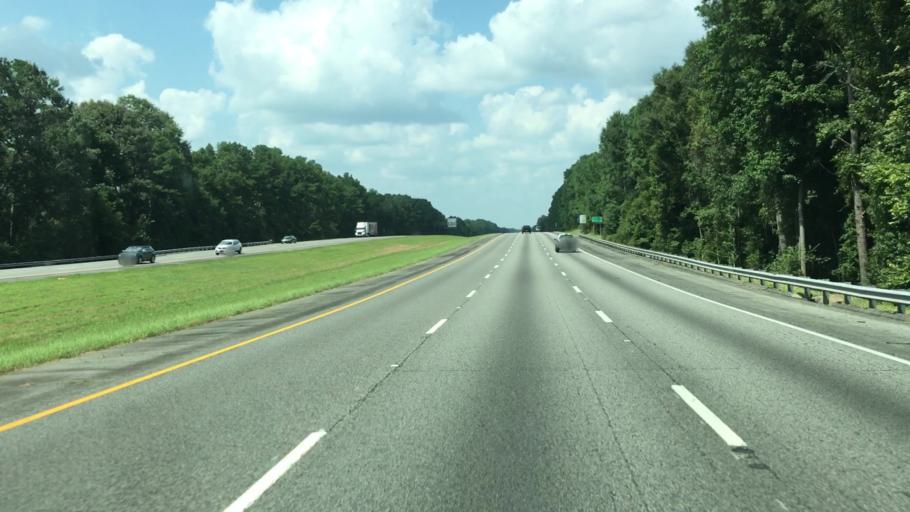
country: US
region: Georgia
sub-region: Dooly County
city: Unadilla
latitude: 32.3487
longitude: -83.7685
